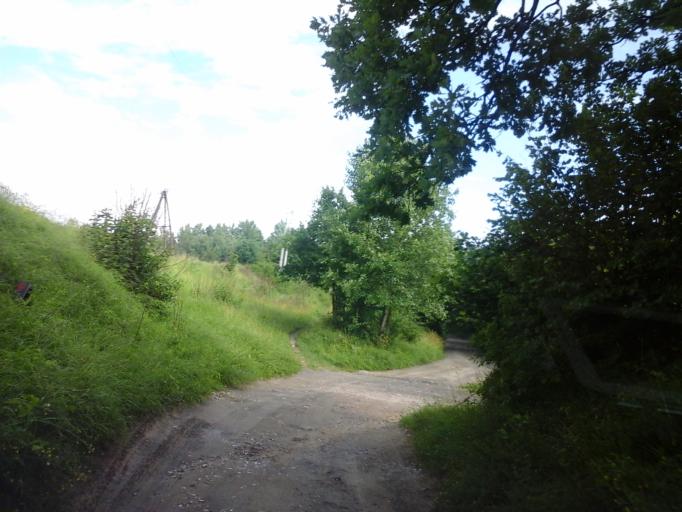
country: PL
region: West Pomeranian Voivodeship
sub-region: Powiat choszczenski
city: Choszczno
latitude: 53.1483
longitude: 15.4319
